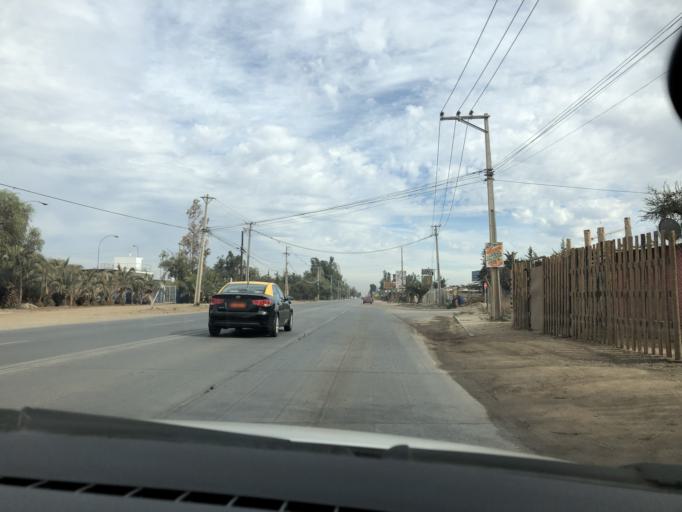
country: CL
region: Santiago Metropolitan
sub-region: Provincia de Cordillera
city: Puente Alto
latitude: -33.5976
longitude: -70.5014
